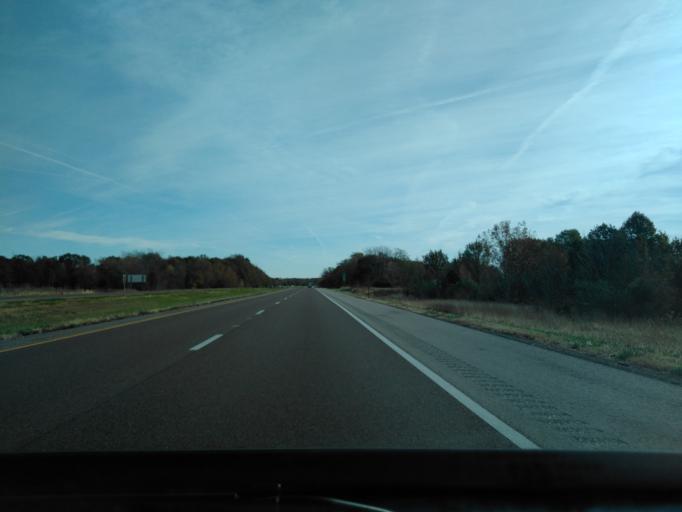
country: US
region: Illinois
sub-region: Madison County
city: Saint Jacob
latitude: 38.7643
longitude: -89.7750
